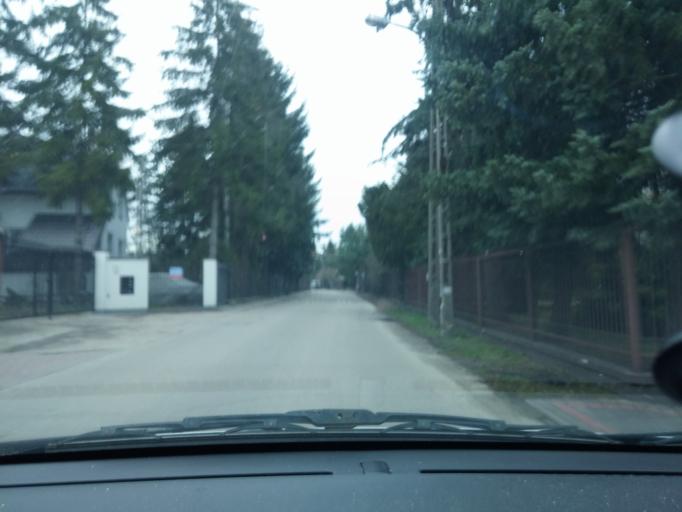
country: PL
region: Masovian Voivodeship
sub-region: Warszawa
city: Wawer
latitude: 52.1980
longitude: 21.1305
